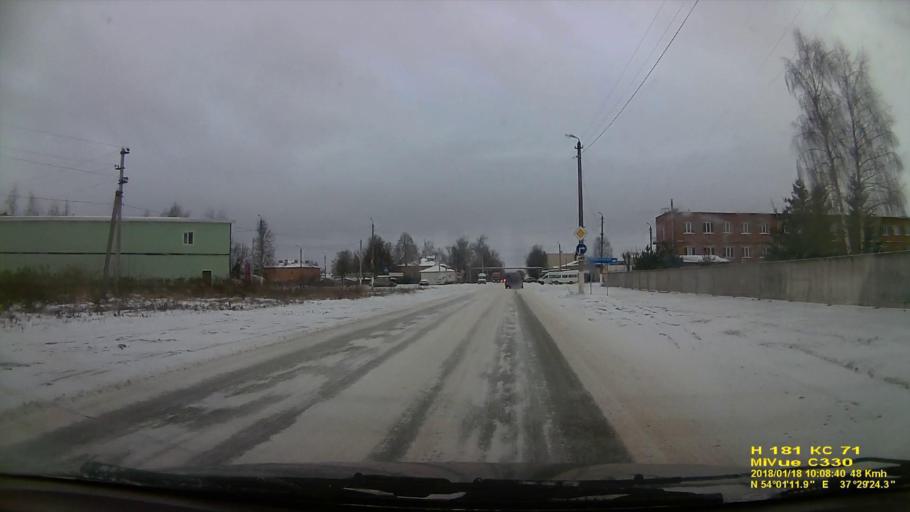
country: RU
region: Tula
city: Pervomayskiy
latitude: 54.0199
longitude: 37.4902
